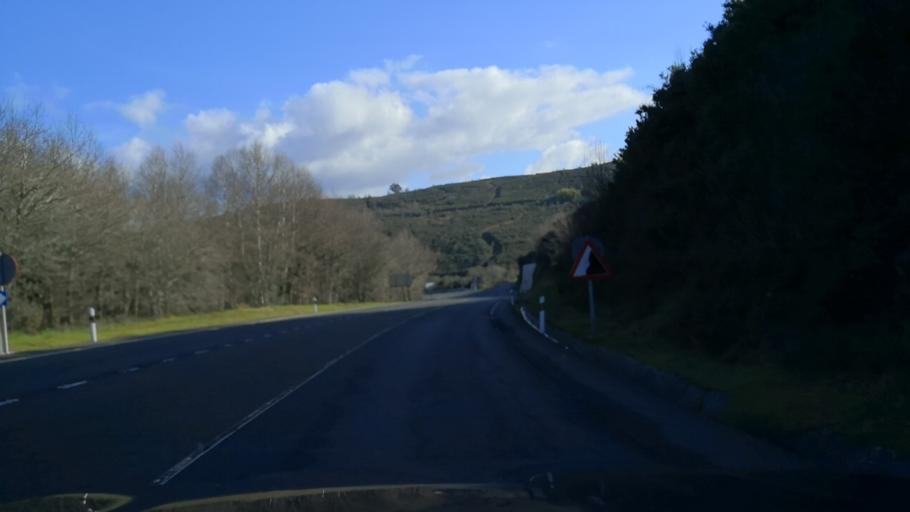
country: ES
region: Galicia
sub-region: Provincia de Pontevedra
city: Silleda
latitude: 42.7004
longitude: -8.3394
